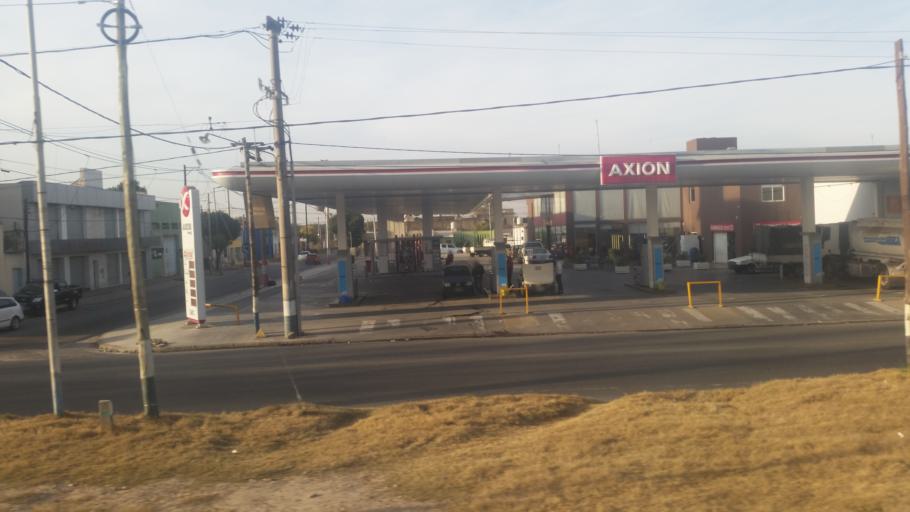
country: AR
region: Cordoba
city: Malvinas Argentinas
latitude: -31.4617
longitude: -64.1065
